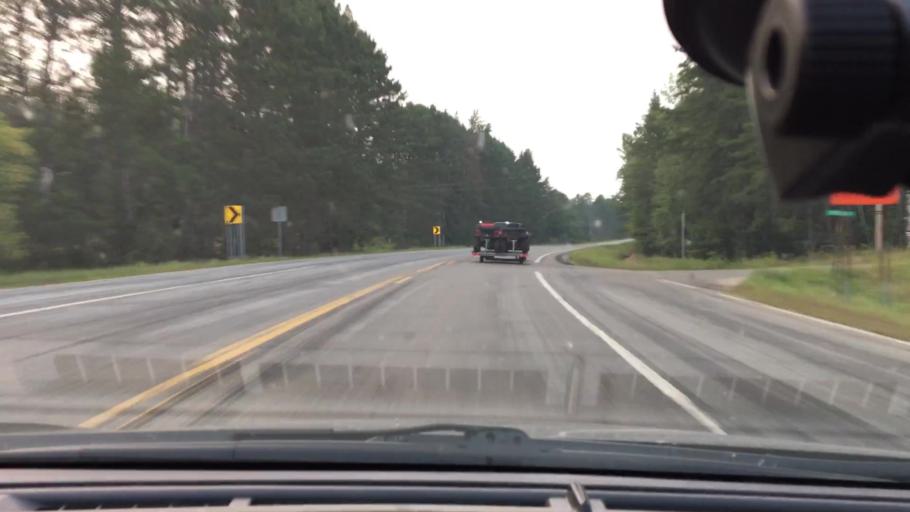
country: US
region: Minnesota
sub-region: Crow Wing County
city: Cross Lake
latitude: 46.7434
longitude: -93.9667
